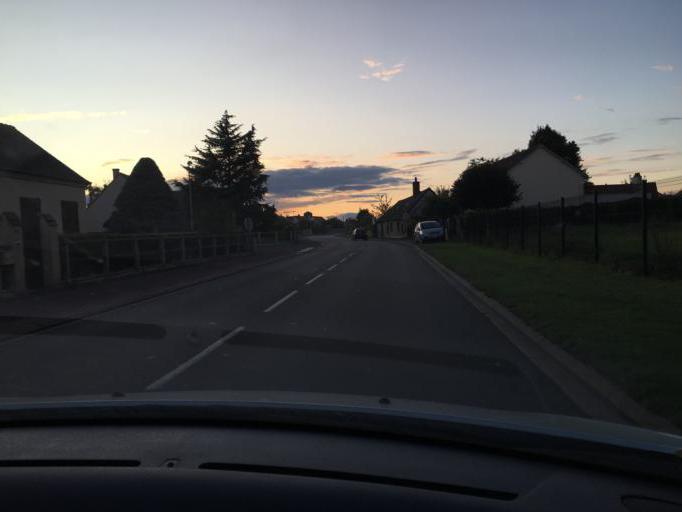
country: FR
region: Centre
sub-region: Departement d'Eure-et-Loir
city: Brou
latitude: 48.2145
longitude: 1.1736
